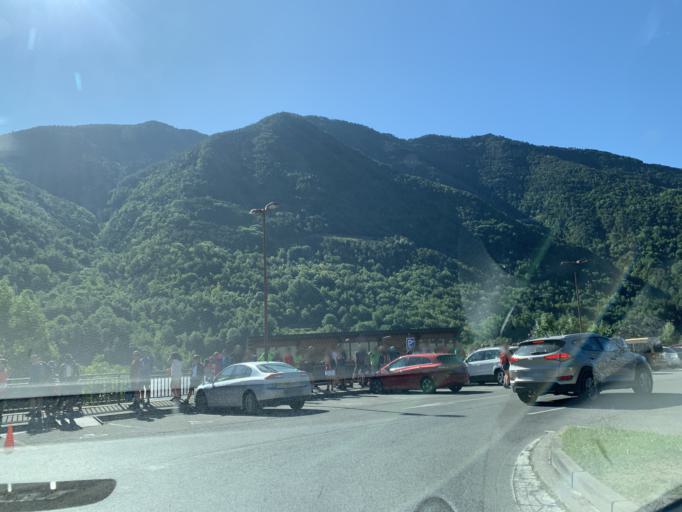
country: ES
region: Aragon
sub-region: Provincia de Huesca
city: Broto
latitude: 42.6261
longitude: -0.1117
